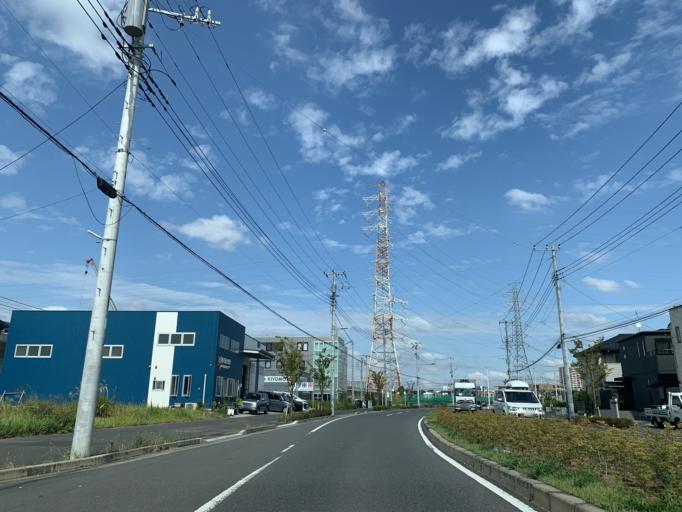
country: JP
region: Chiba
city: Nagareyama
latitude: 35.8600
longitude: 139.9167
